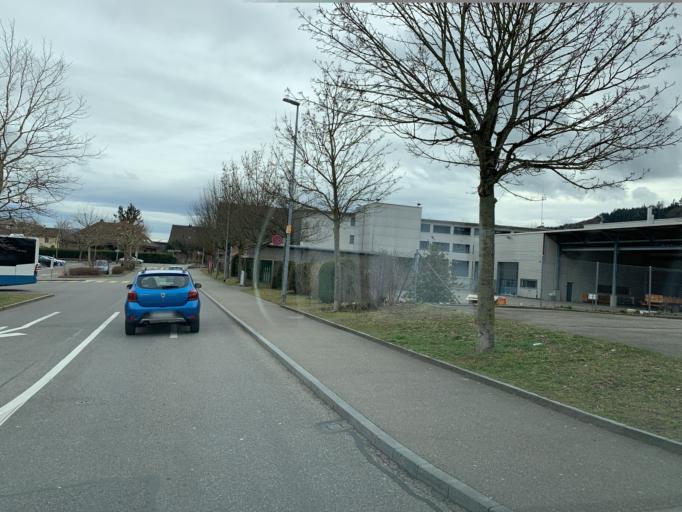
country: CH
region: Aargau
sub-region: Bezirk Baden
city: Spreitenbach
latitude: 47.4207
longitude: 8.3681
